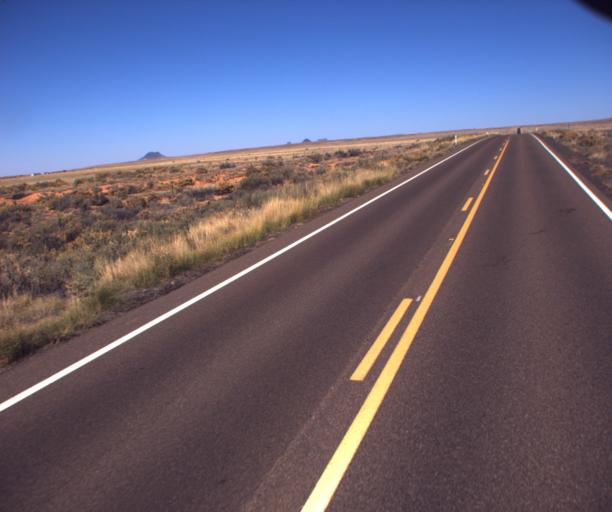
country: US
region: Arizona
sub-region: Navajo County
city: Dilkon
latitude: 35.2578
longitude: -110.4297
